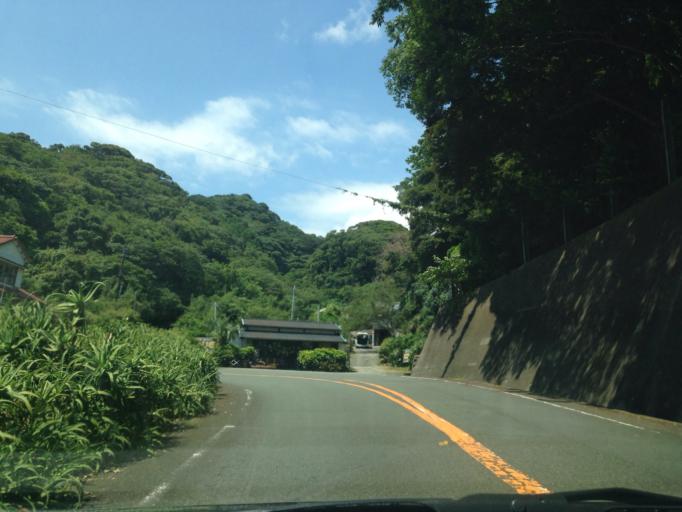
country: JP
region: Shizuoka
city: Shimoda
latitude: 34.6127
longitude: 138.8406
